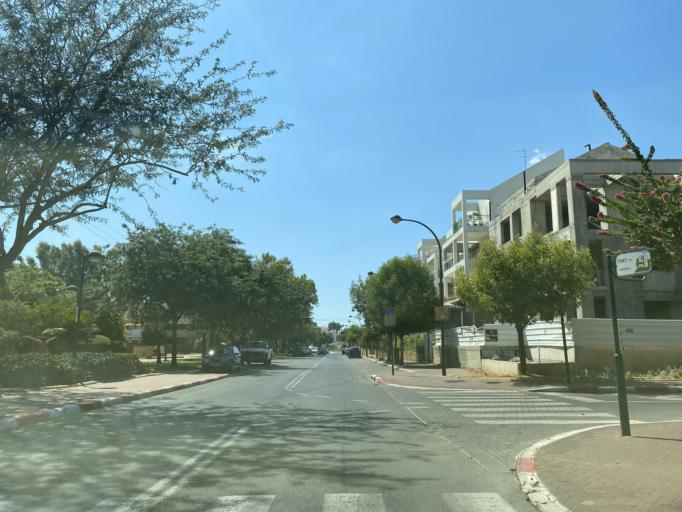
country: IL
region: Central District
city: Ra'anana
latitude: 32.1882
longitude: 34.8853
